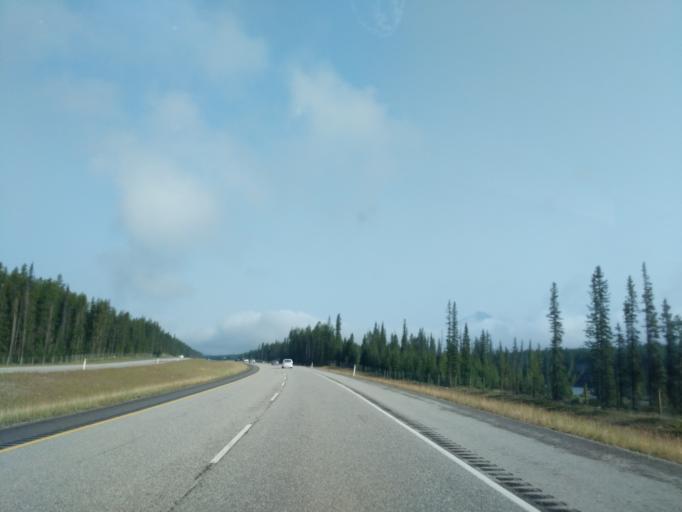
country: CA
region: Alberta
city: Lake Louise
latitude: 51.3334
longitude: -116.0563
